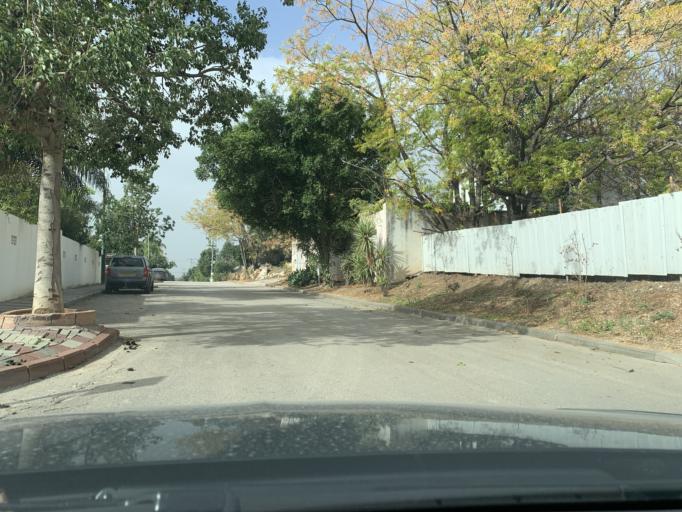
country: IL
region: Central District
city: Jaljulya
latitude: 32.1579
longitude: 34.9439
